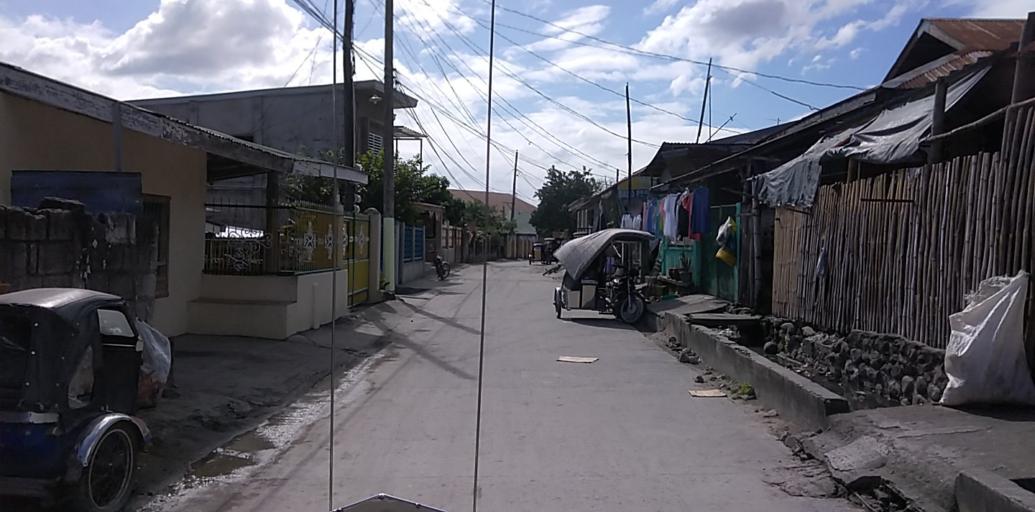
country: PH
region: Central Luzon
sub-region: Province of Pampanga
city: Porac
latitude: 15.0772
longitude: 120.5319
